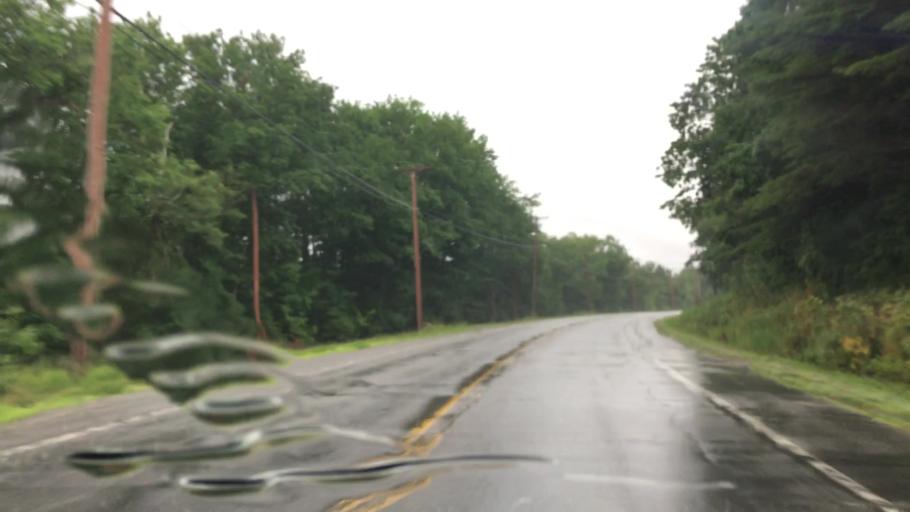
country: US
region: Maine
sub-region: Kennebec County
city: Pittston
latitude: 44.2186
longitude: -69.7628
